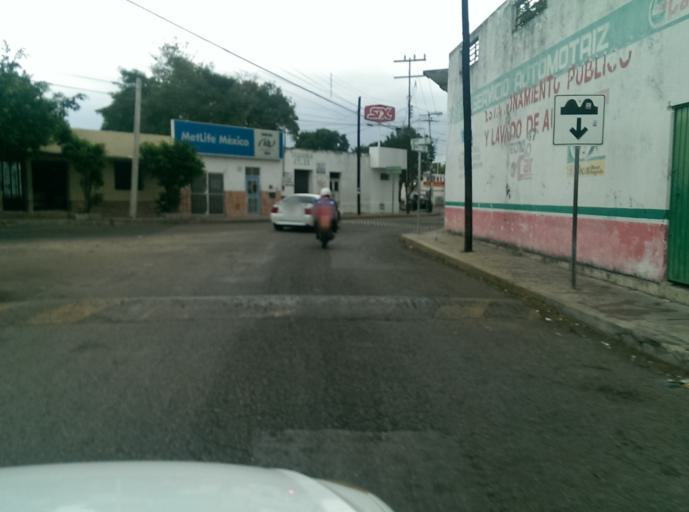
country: MX
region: Yucatan
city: Merida
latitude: 20.9791
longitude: -89.6385
